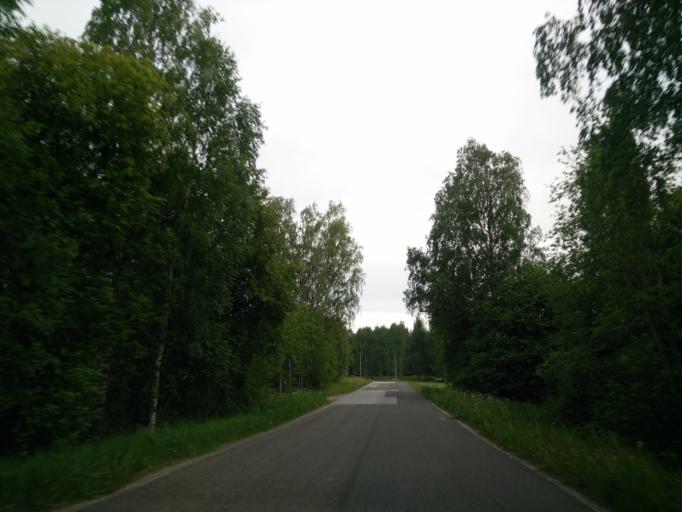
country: SE
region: Vaesternorrland
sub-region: Kramfors Kommun
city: Kramfors
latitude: 63.0471
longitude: 17.7997
